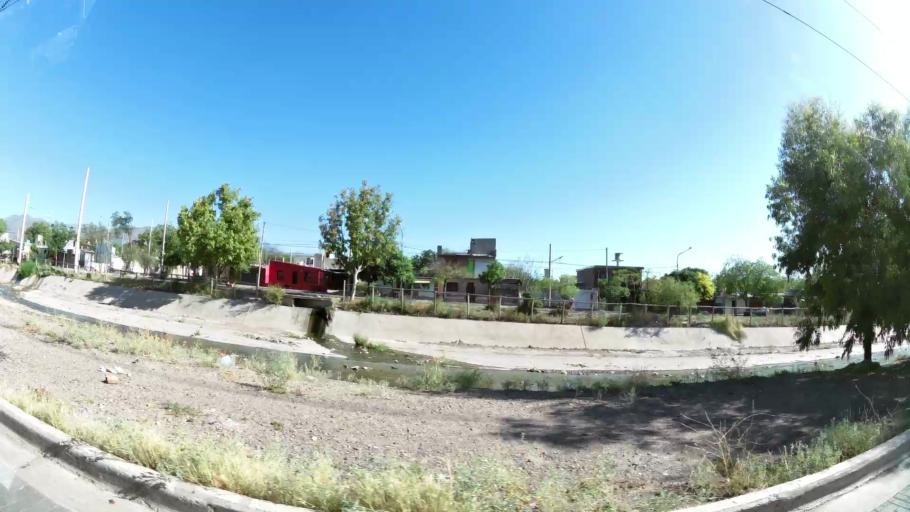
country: AR
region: Mendoza
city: Las Heras
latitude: -32.8715
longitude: -68.8652
